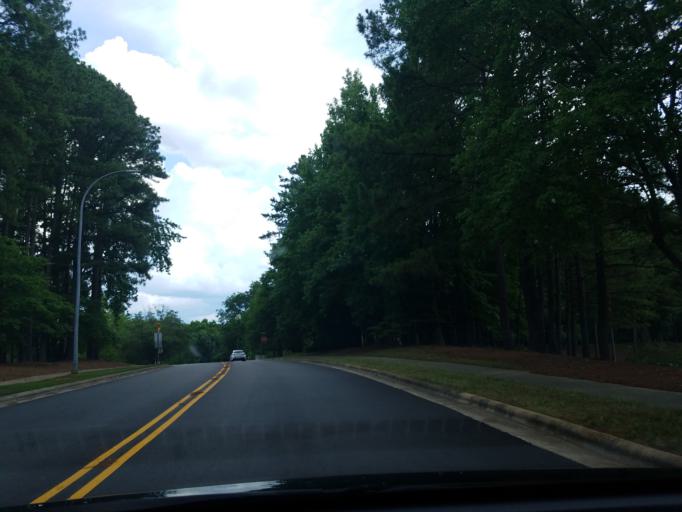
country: US
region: North Carolina
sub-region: Wake County
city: Apex
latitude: 35.7330
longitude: -78.8072
